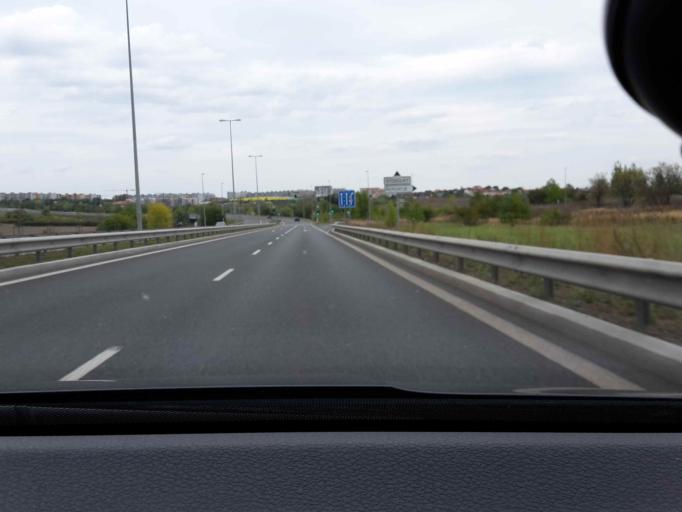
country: CZ
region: Central Bohemia
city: Hostivice
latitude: 50.0377
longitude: 14.2966
